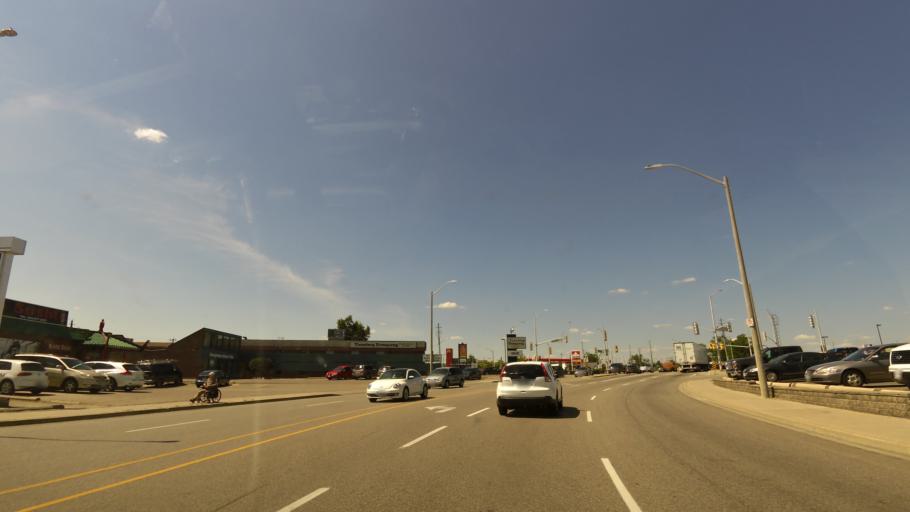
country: CA
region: Ontario
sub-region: Halton
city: Milton
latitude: 43.6496
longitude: -79.9029
